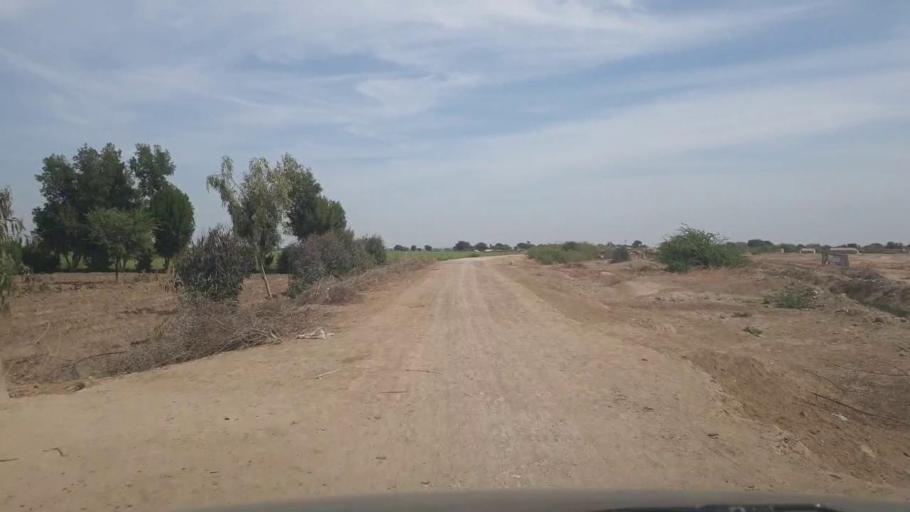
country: PK
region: Sindh
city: Kunri
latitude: 25.2400
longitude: 69.6406
